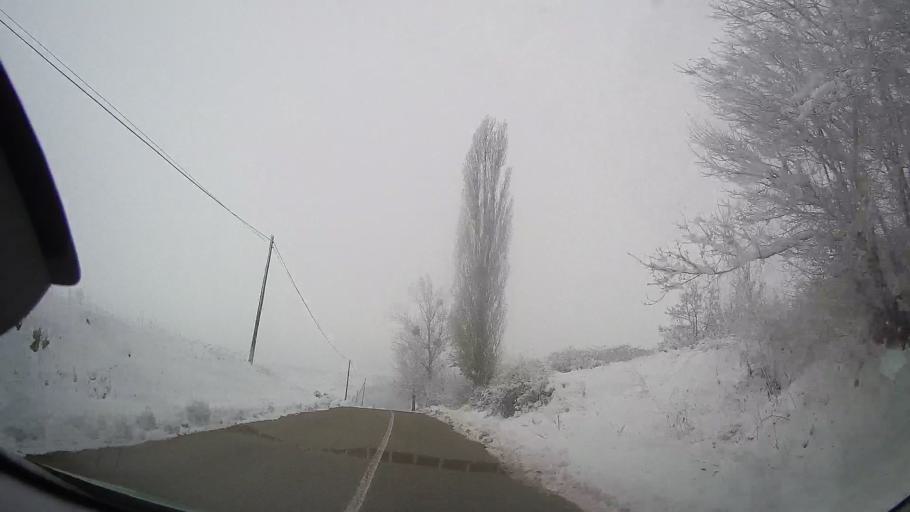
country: RO
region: Neamt
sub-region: Comuna Bozieni
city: Bozieni
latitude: 46.8451
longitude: 27.1687
